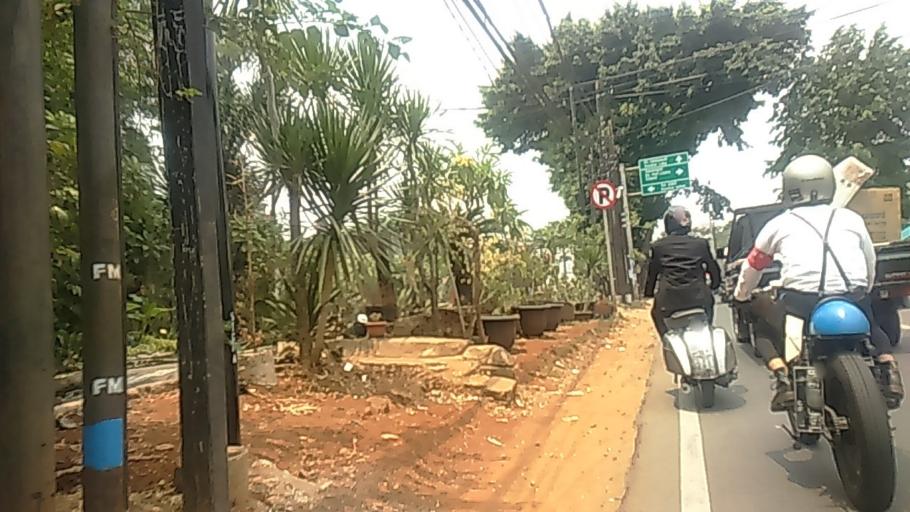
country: ID
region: West Java
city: Pamulang
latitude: -6.2997
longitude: 106.7772
